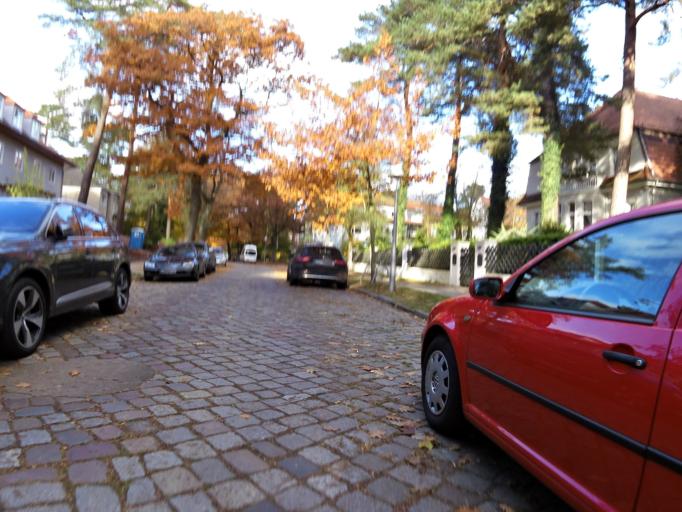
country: DE
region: Berlin
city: Zehlendorf Bezirk
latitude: 52.4413
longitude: 13.2307
